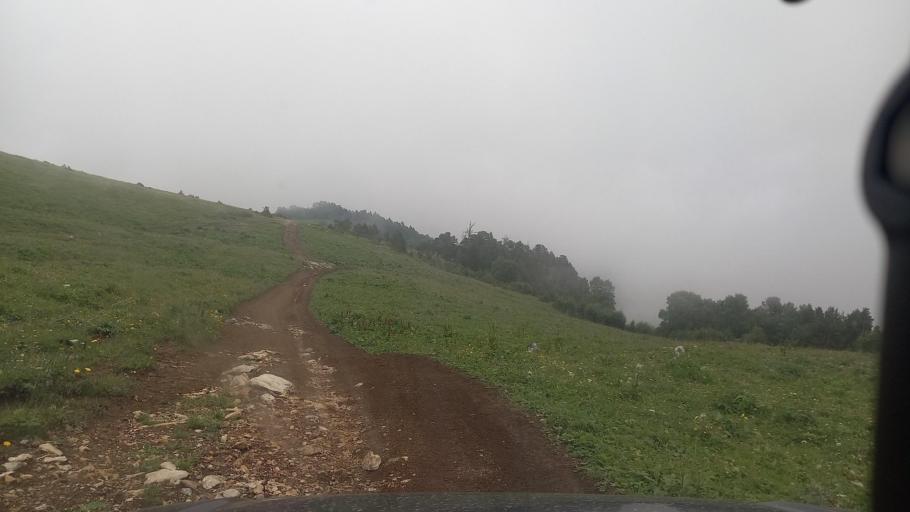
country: RU
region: Karachayevo-Cherkesiya
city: Kurdzhinovo
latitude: 43.7932
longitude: 40.8383
